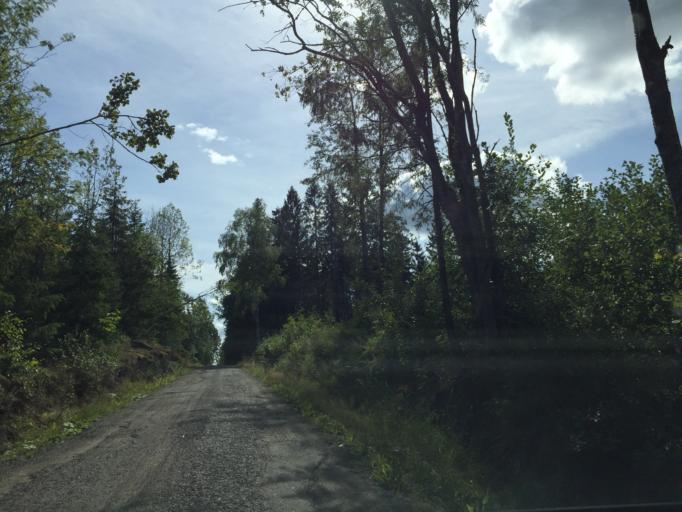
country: NO
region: Vestfold
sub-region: Hof
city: Hof
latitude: 59.4474
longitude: 10.1555
